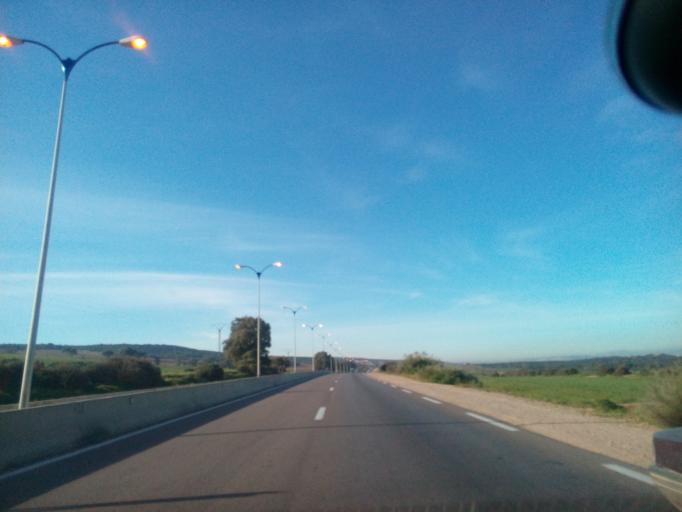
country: DZ
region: Mostaganem
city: Mostaganem
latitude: 35.8139
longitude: -0.0299
